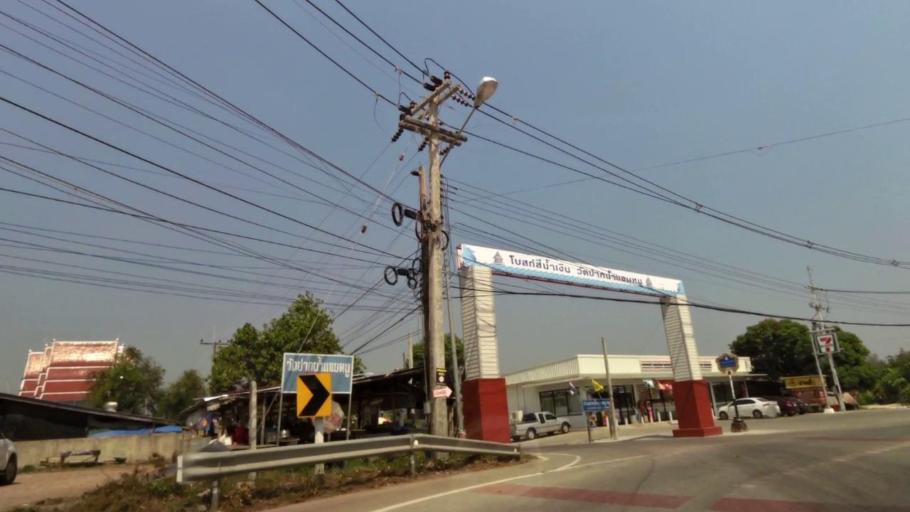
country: TH
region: Chanthaburi
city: Tha Mai
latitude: 12.5406
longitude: 101.9519
